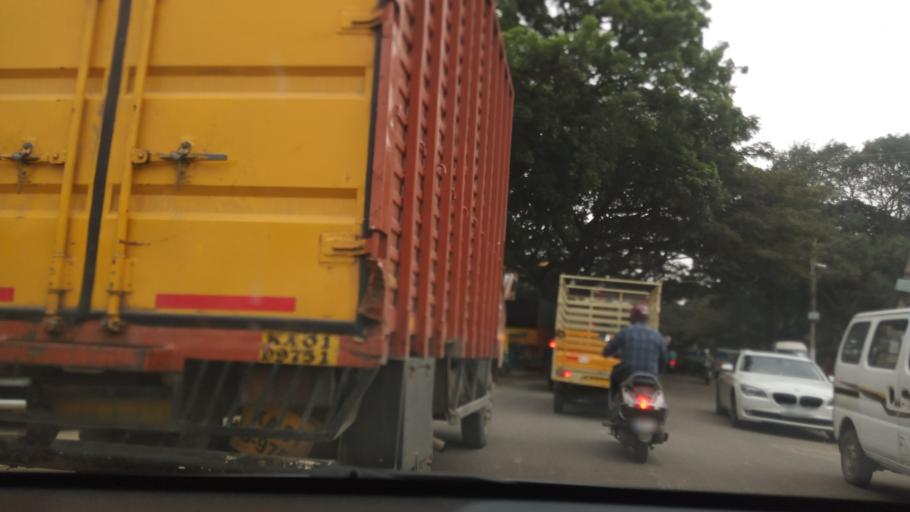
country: IN
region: Karnataka
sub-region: Bangalore Urban
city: Bangalore
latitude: 13.0217
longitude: 77.5351
